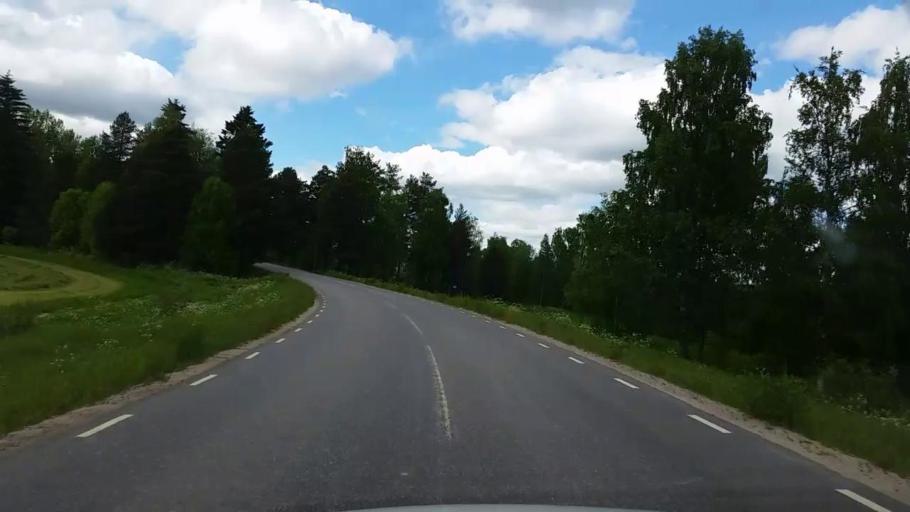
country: SE
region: Gaevleborg
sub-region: Ovanakers Kommun
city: Alfta
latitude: 61.3897
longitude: 16.0478
